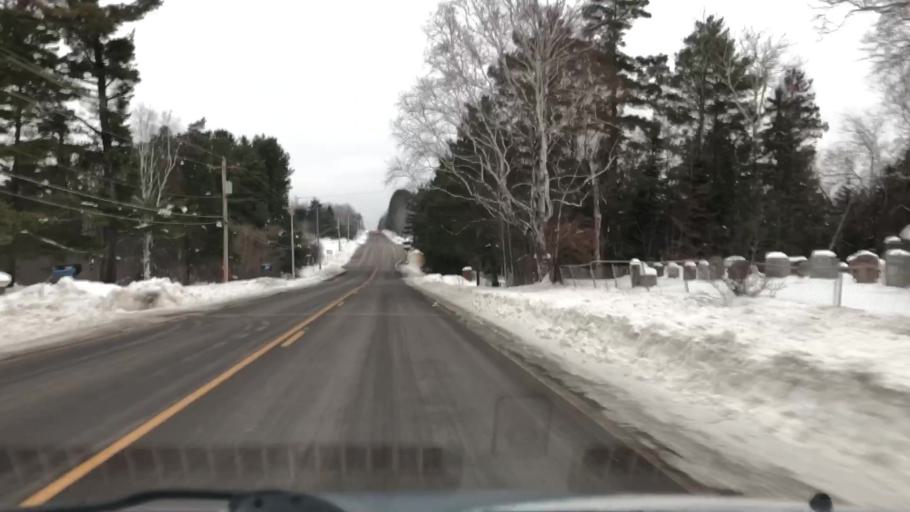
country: US
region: Minnesota
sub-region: Saint Louis County
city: Arnold
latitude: 46.8628
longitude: -92.1111
